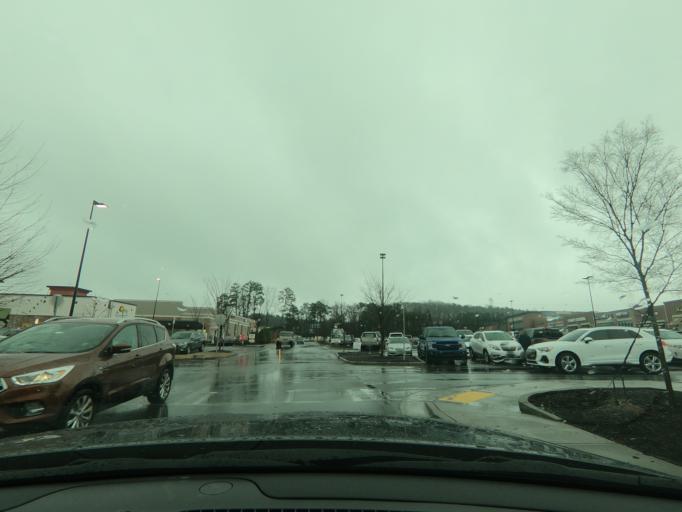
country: US
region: Georgia
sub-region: Cobb County
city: Kennesaw
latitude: 33.9991
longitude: -84.5903
